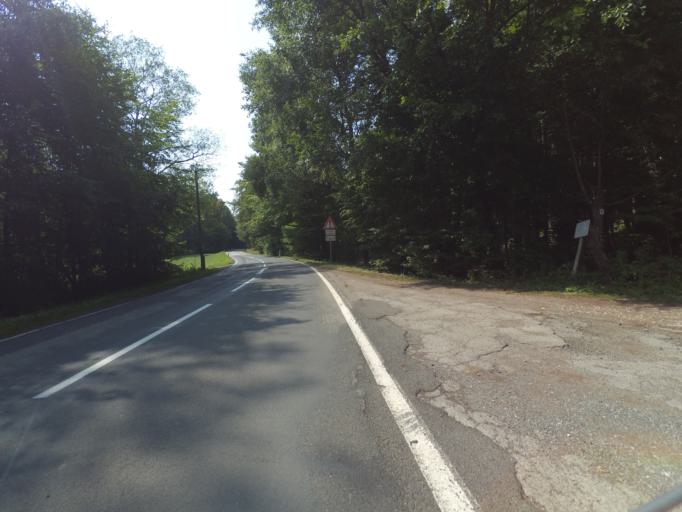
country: DE
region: Saarland
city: Britten
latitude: 49.5205
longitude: 6.6640
